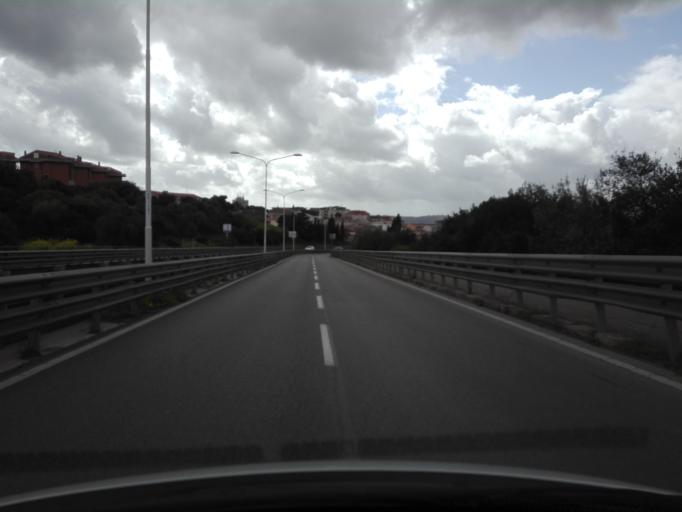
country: IT
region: Sardinia
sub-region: Provincia di Sassari
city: Sassari
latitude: 40.7313
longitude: 8.5748
